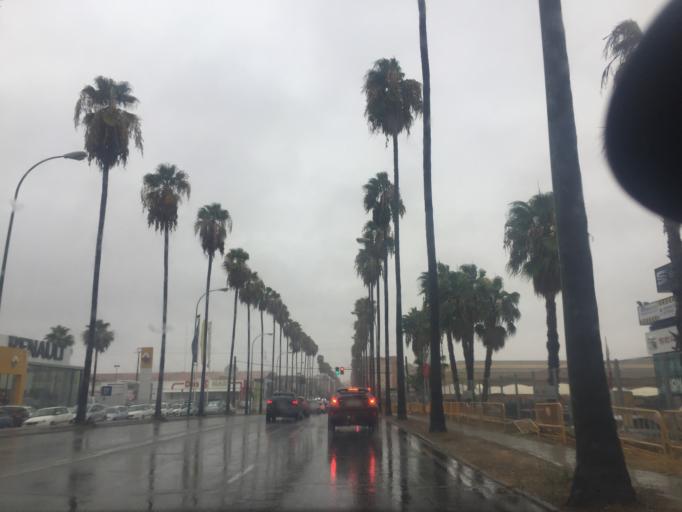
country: ES
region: Andalusia
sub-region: Provincia de Sevilla
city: Sevilla
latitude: 37.3635
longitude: -5.9571
